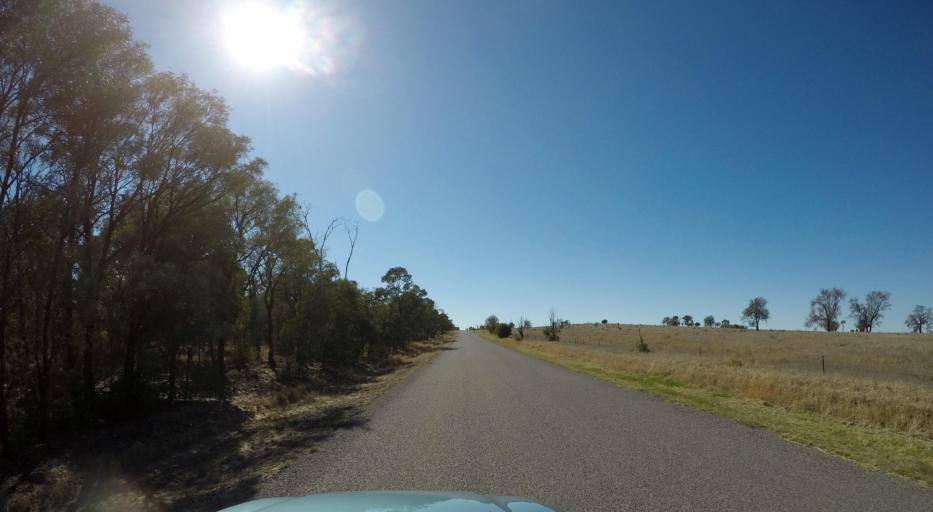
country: AU
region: Queensland
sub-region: Banana
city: Taroom
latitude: -25.7886
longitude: 149.6825
